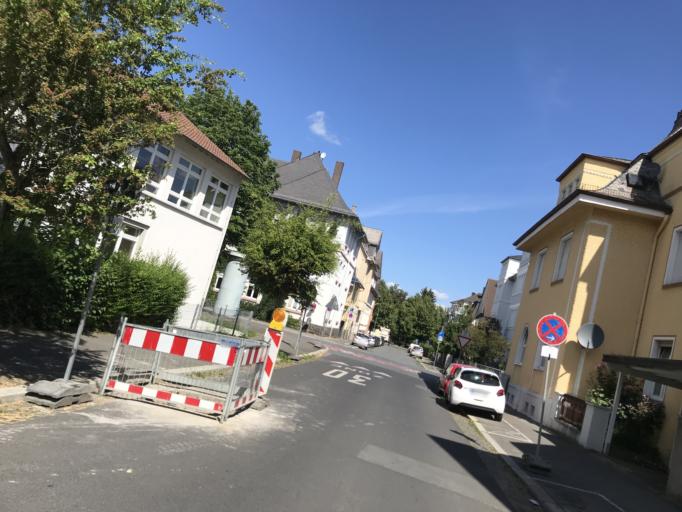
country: DE
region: Hesse
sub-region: Regierungsbezirk Darmstadt
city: Friedberg
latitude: 50.3306
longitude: 8.7555
